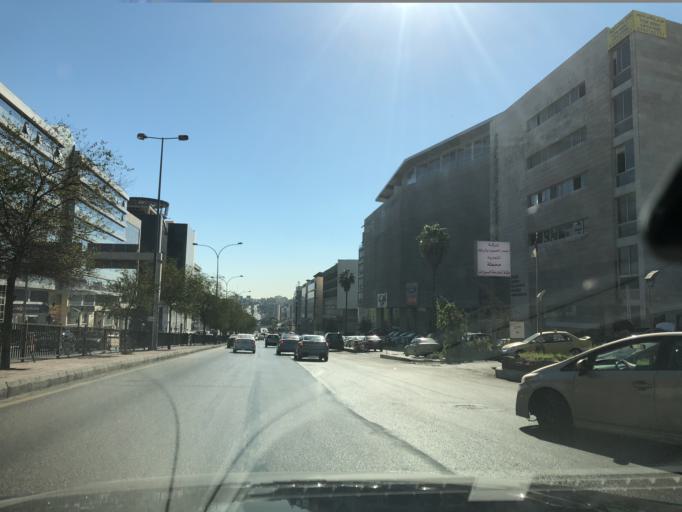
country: JO
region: Amman
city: Wadi as Sir
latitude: 31.9763
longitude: 35.8571
